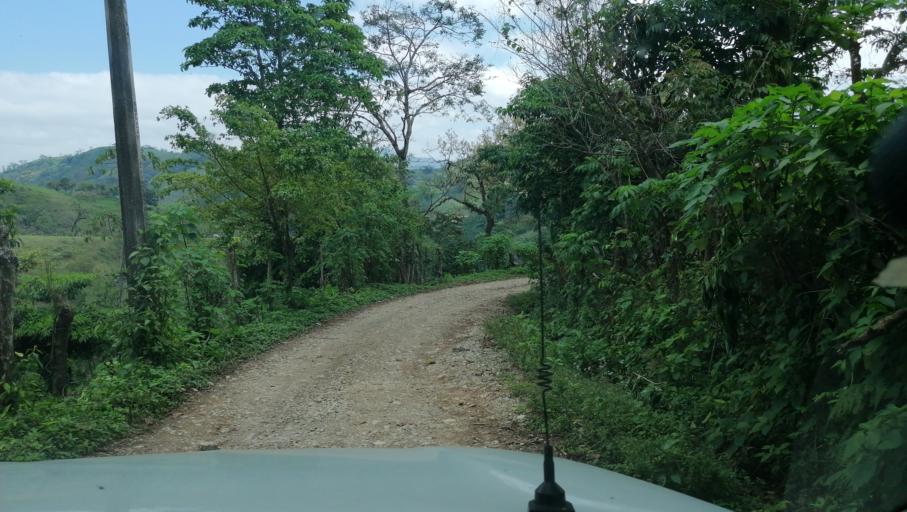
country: MX
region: Chiapas
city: Ixtacomitan
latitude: 17.3584
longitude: -93.1175
